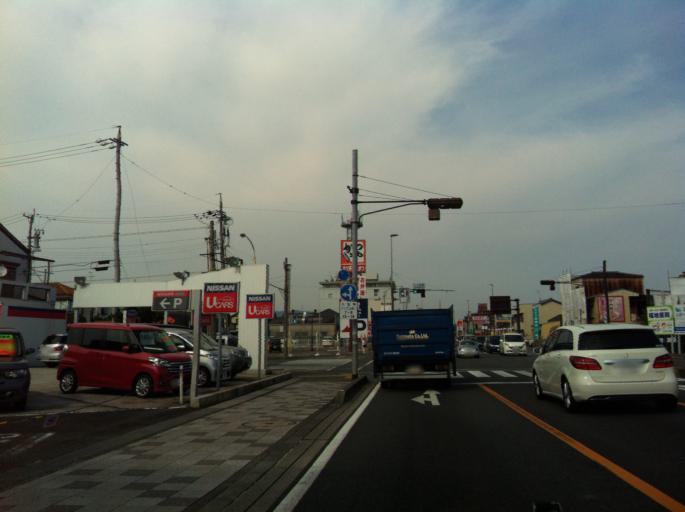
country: JP
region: Shizuoka
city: Shizuoka-shi
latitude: 35.0107
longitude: 138.4492
